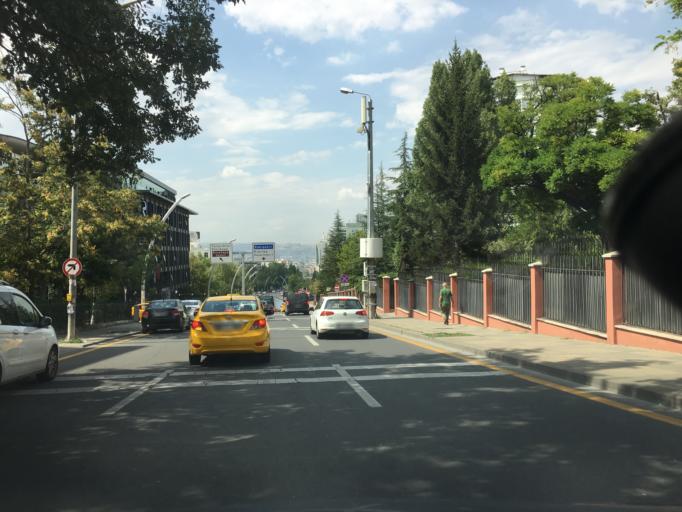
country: TR
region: Ankara
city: Cankaya
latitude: 39.8985
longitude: 32.8610
